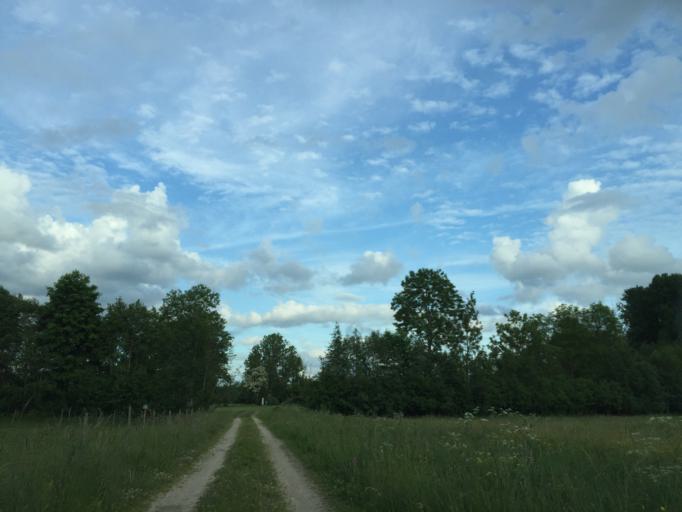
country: LV
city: Tireli
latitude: 56.8353
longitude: 23.5414
